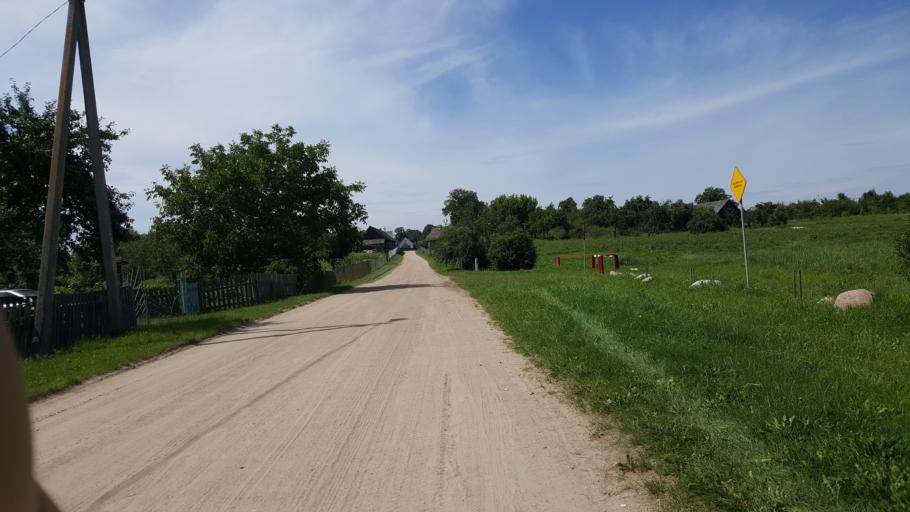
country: BY
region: Brest
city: Pruzhany
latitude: 52.5512
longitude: 24.2217
